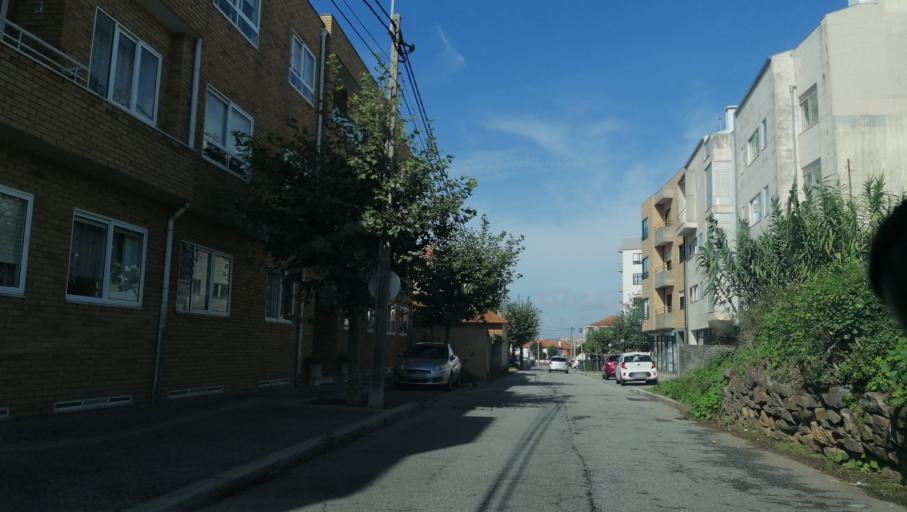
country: PT
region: Aveiro
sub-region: Espinho
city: Espinho
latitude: 41.0098
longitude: -8.6320
